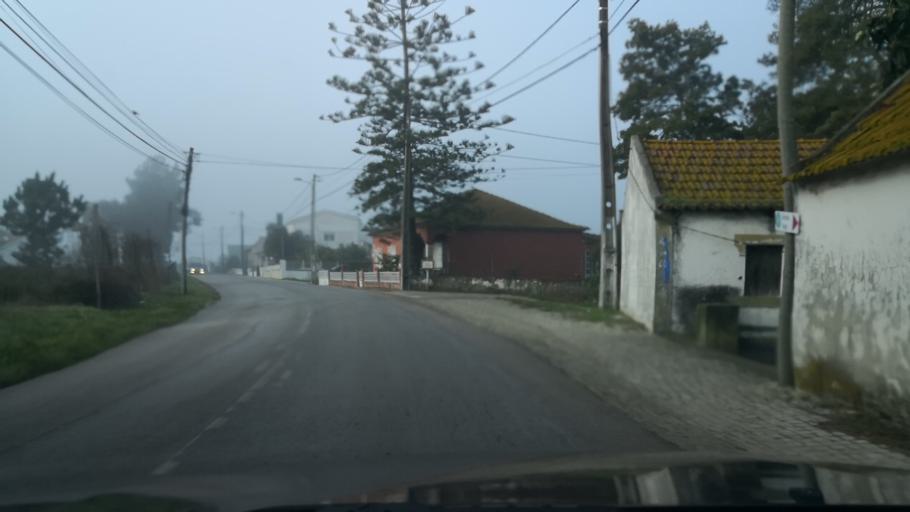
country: PT
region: Setubal
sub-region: Palmela
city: Pinhal Novo
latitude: 38.6036
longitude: -8.8963
